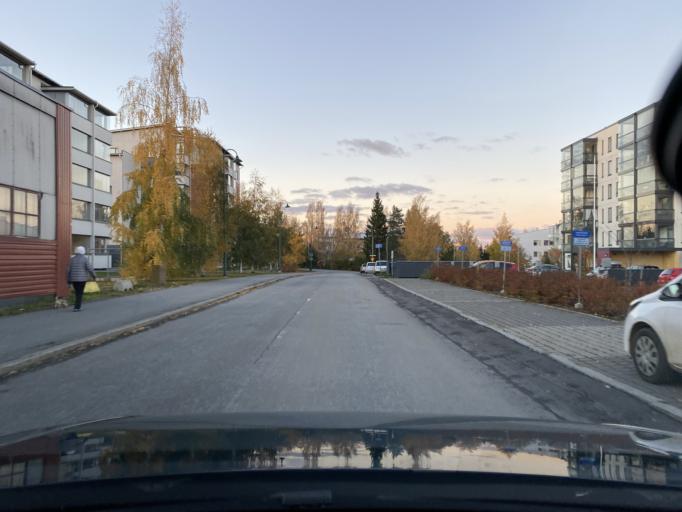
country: FI
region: Pirkanmaa
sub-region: Tampere
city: Lempaeaelae
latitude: 61.3157
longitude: 23.7576
